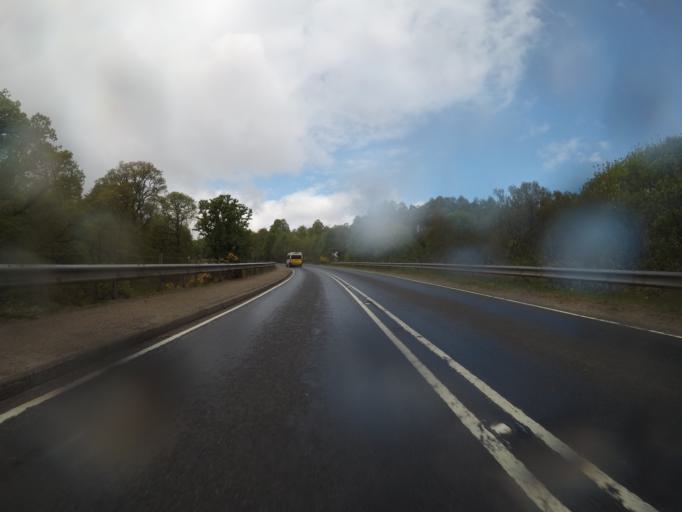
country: GB
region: Scotland
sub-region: Highland
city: Spean Bridge
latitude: 56.8944
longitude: -4.9307
